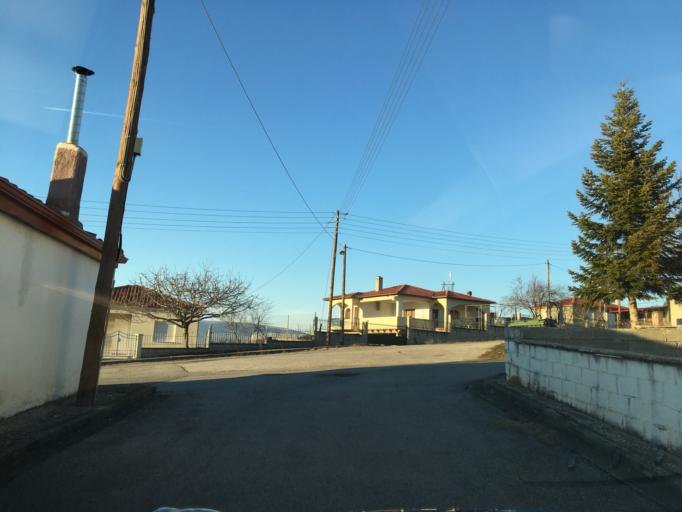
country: GR
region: West Macedonia
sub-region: Nomos Kozanis
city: Kozani
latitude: 40.2928
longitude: 21.7364
